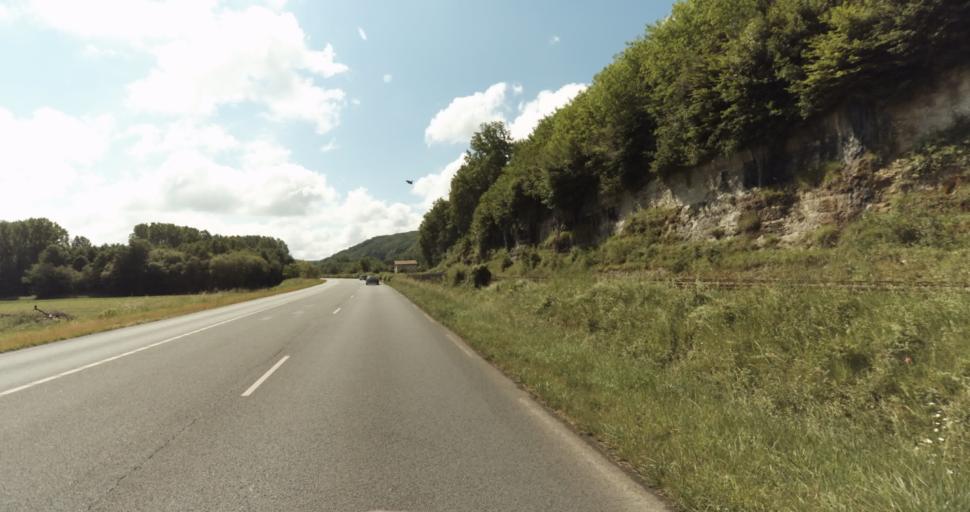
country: FR
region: Aquitaine
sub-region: Departement de la Dordogne
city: Belves
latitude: 44.8290
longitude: 0.9445
